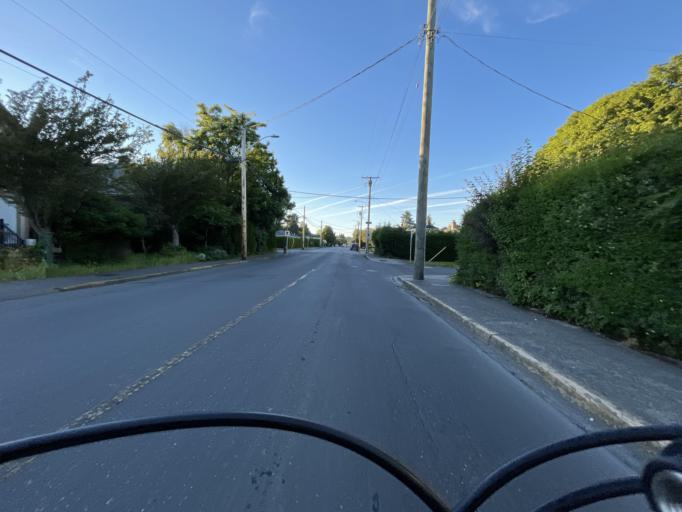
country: CA
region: British Columbia
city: Oak Bay
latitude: 48.4280
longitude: -123.3226
